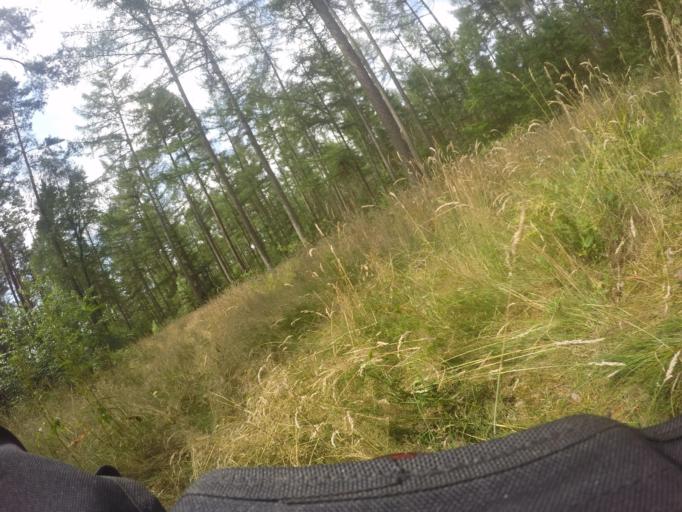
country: DE
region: Lower Saxony
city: Dahlem
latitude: 53.2369
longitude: 10.7440
